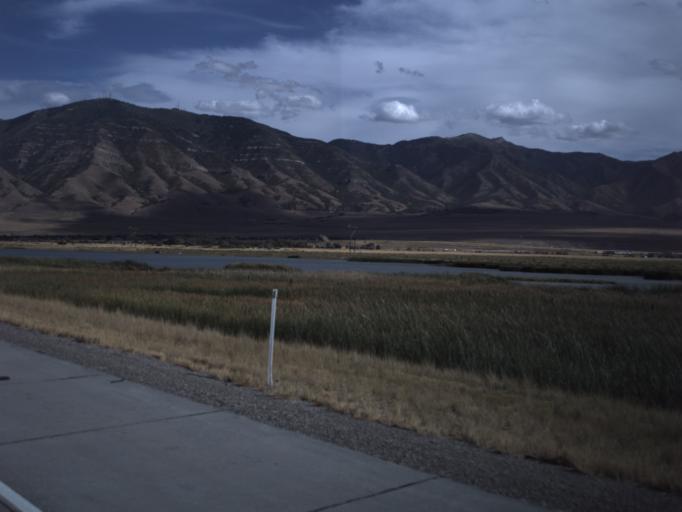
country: US
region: Utah
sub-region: Tooele County
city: Stansbury park
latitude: 40.6649
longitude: -112.3149
